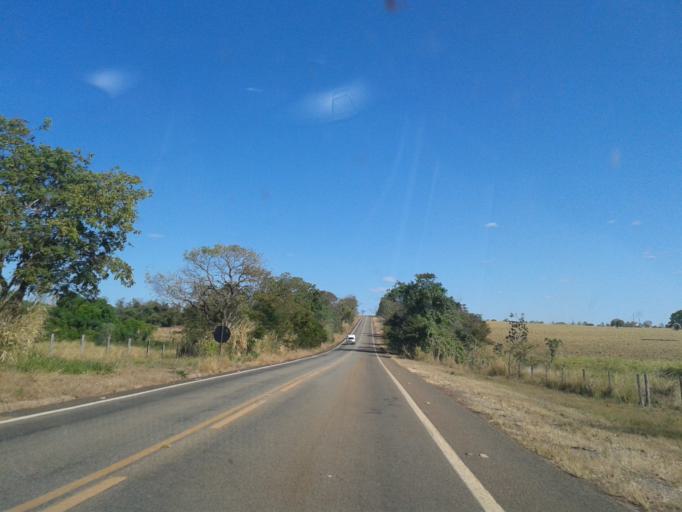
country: BR
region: Goias
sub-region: Crixas
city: Crixas
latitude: -14.2399
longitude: -50.3953
